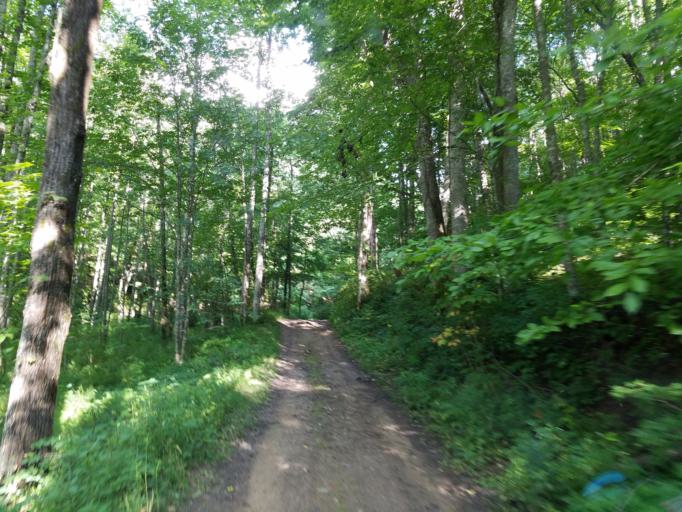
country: US
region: Georgia
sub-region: Lumpkin County
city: Dahlonega
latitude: 34.6855
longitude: -84.0518
